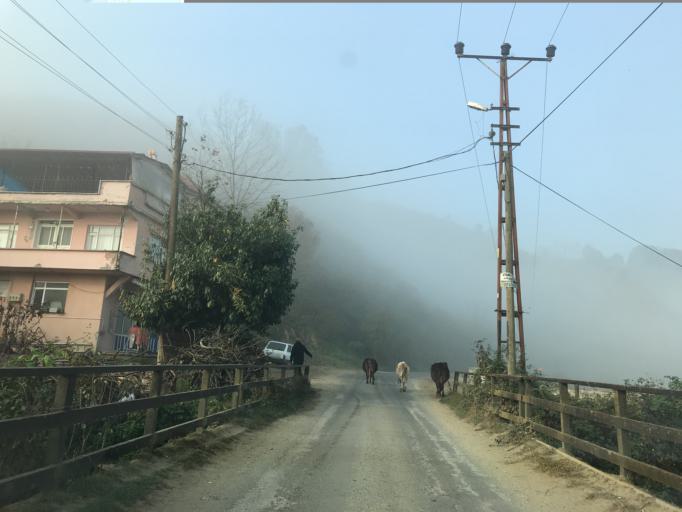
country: TR
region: Duzce
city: Cumayeri
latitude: 40.9079
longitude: 30.9490
